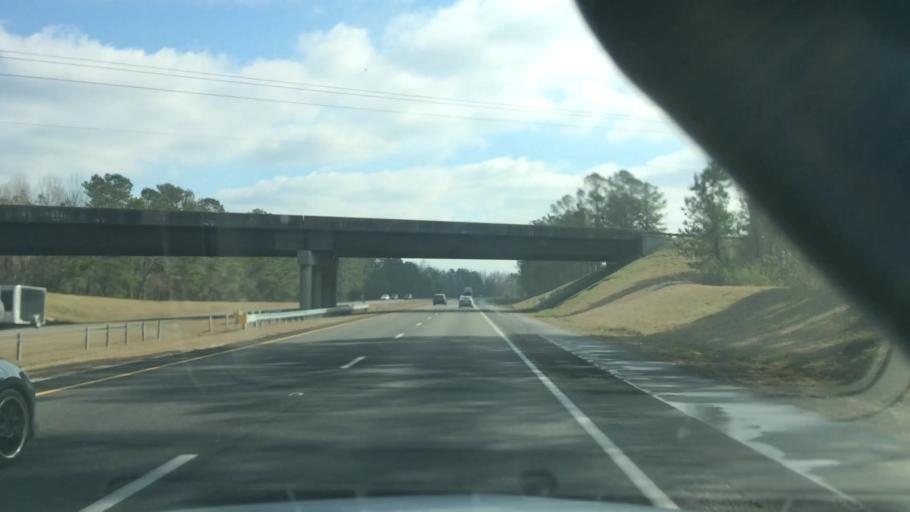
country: US
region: North Carolina
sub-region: Pender County
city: Burgaw
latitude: 34.6123
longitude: -77.9210
